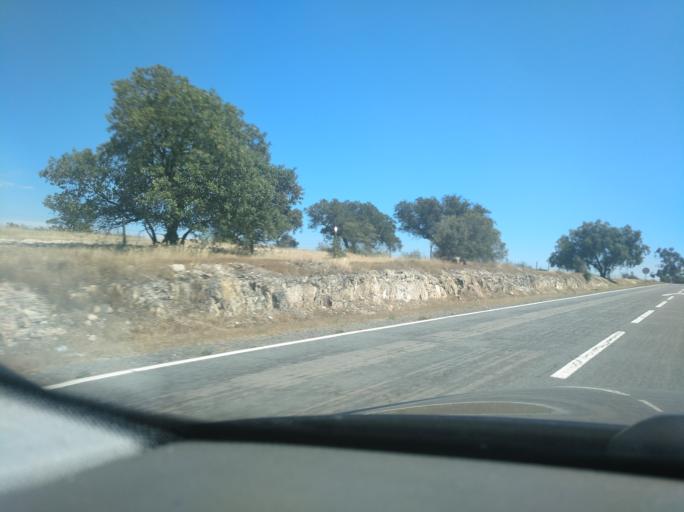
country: PT
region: Beja
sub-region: Castro Verde
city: Castro Verde
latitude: 37.6279
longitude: -8.0821
